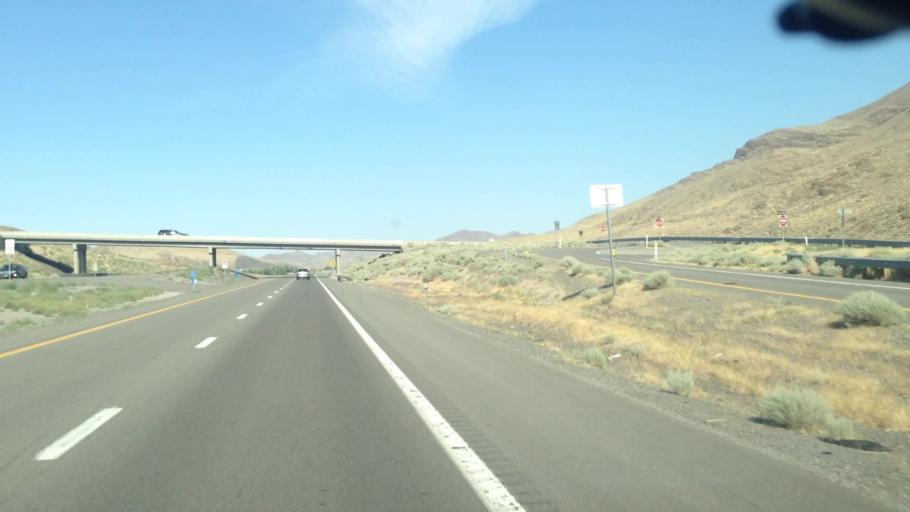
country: US
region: Nevada
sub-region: Lyon County
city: Fernley
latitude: 39.5891
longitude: -119.4308
